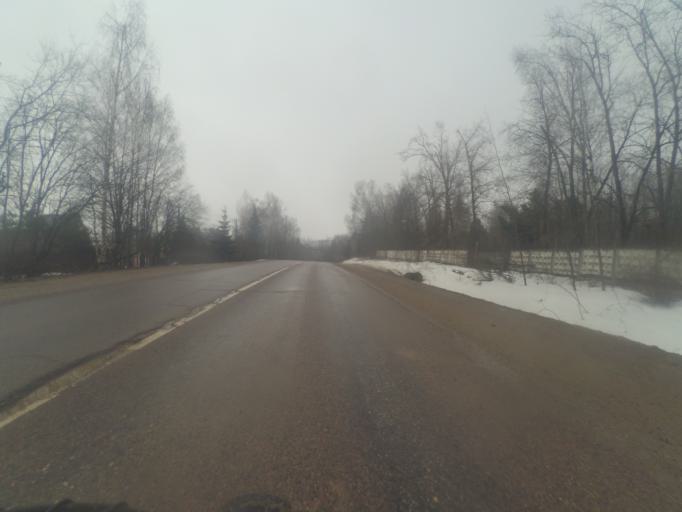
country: RU
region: Moskovskaya
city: Avtopoligon
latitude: 56.2634
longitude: 37.2185
